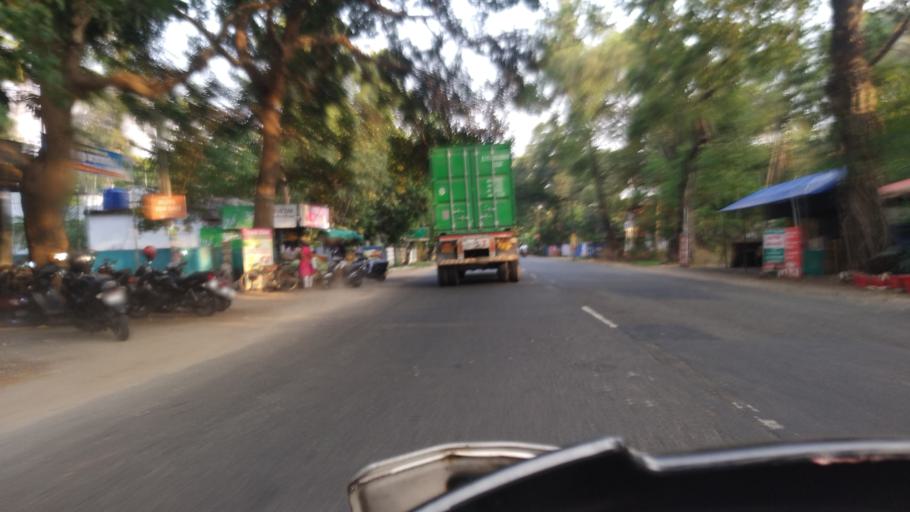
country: IN
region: Kerala
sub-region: Thrissur District
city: Thanniyam
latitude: 10.3435
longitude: 76.1355
